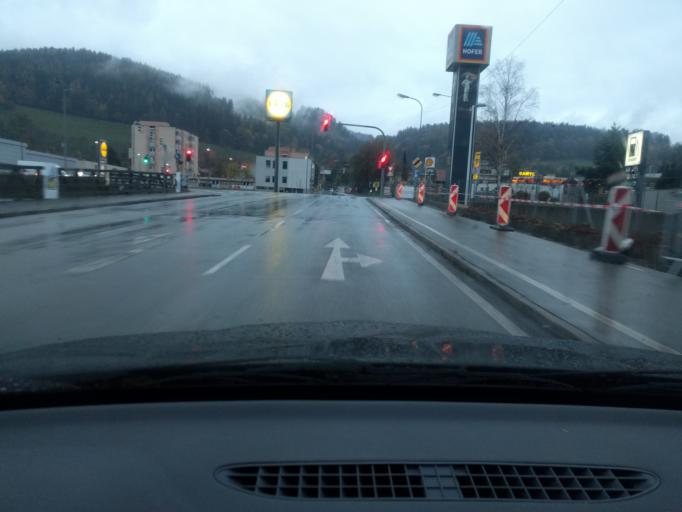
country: AT
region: Styria
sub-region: Politischer Bezirk Leoben
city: Leoben
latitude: 47.3819
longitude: 15.1069
